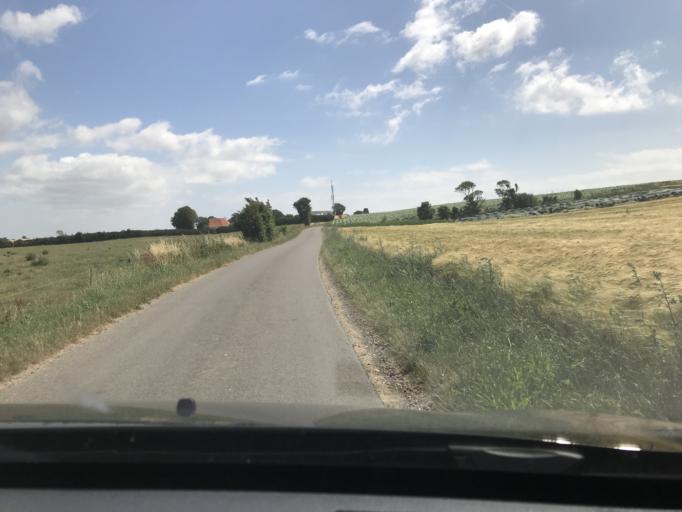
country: DK
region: South Denmark
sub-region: AEro Kommune
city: AEroskobing
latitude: 54.9053
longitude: 10.3041
